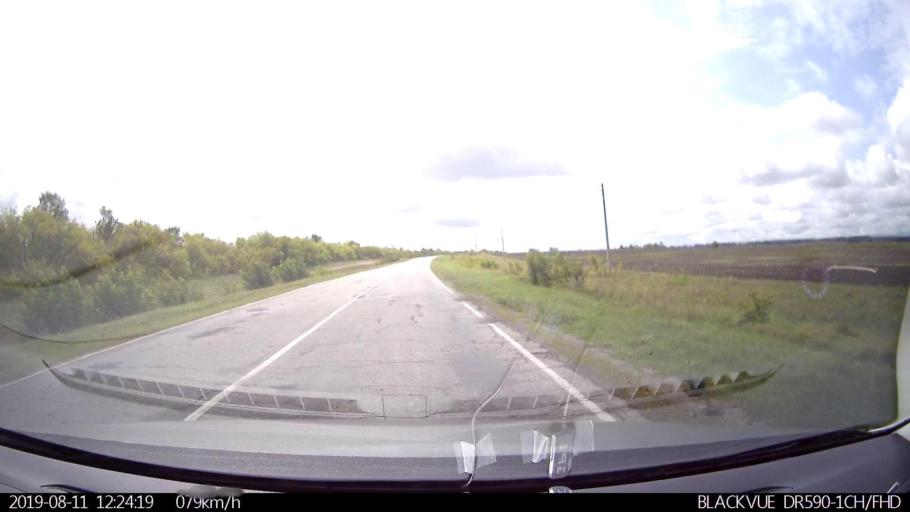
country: RU
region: Ulyanovsk
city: Ignatovka
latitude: 53.8846
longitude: 47.9493
